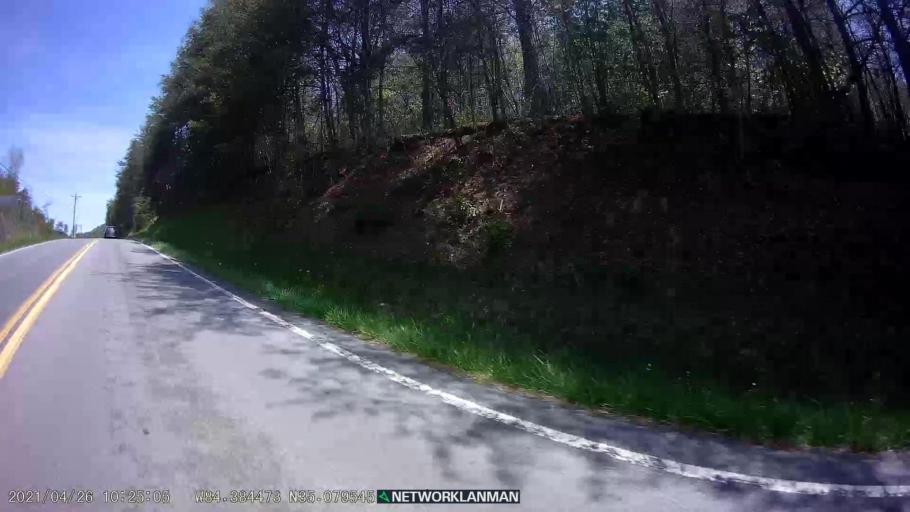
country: US
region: Georgia
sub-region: Fannin County
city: McCaysville
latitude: 35.0798
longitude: -84.3846
